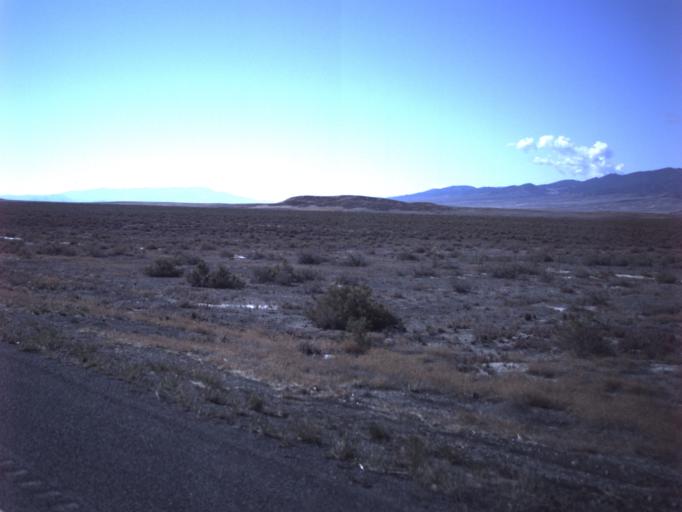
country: US
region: Utah
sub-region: Sanpete County
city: Gunnison
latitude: 39.1913
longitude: -111.8430
